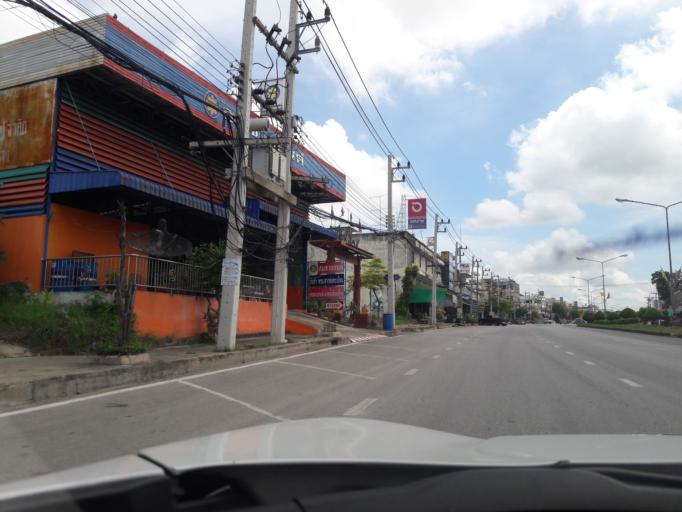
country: TH
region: Lop Buri
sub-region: Amphoe Tha Luang
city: Tha Luang
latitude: 15.0718
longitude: 101.1073
